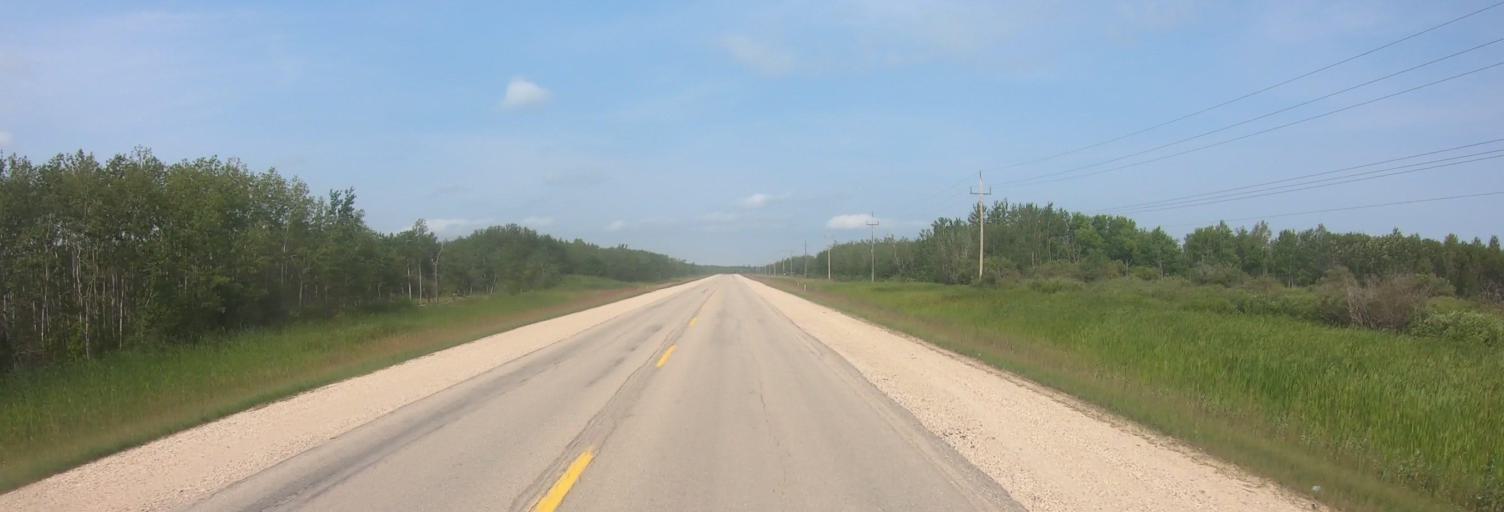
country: CA
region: Manitoba
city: Steinbach
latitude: 49.3528
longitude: -96.6554
